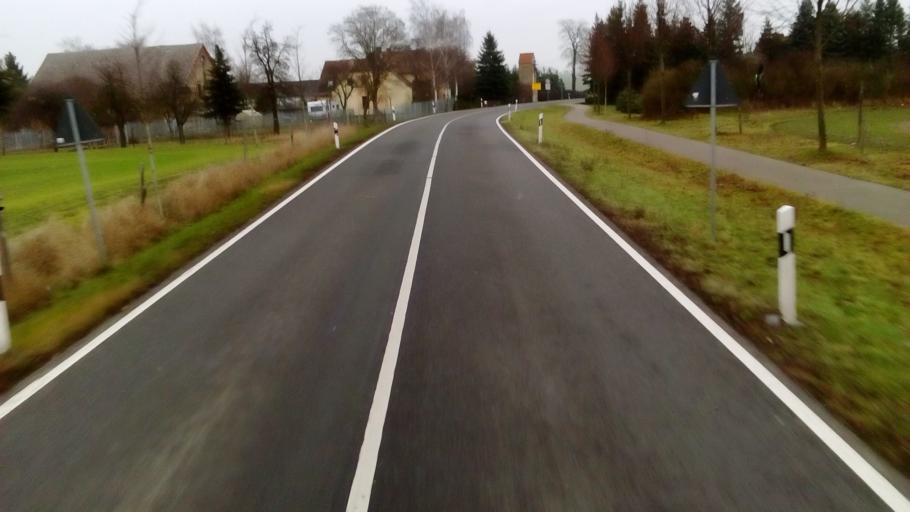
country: DE
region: Mecklenburg-Vorpommern
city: Strasburg
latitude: 53.4920
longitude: 13.8036
